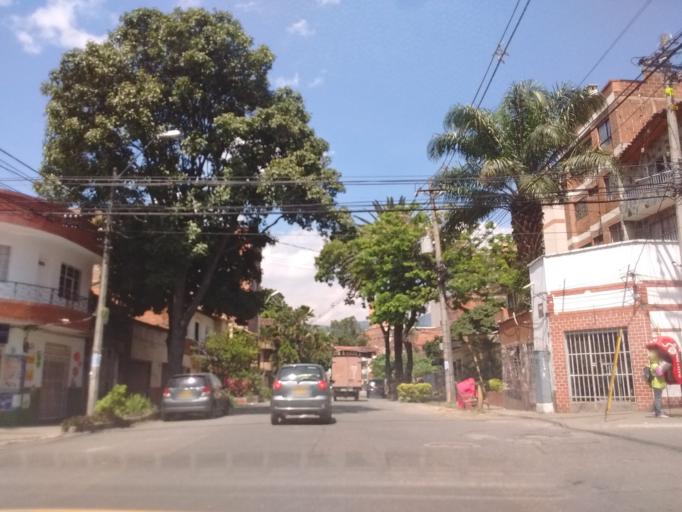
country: CO
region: Antioquia
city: Medellin
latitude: 6.2534
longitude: -75.6035
